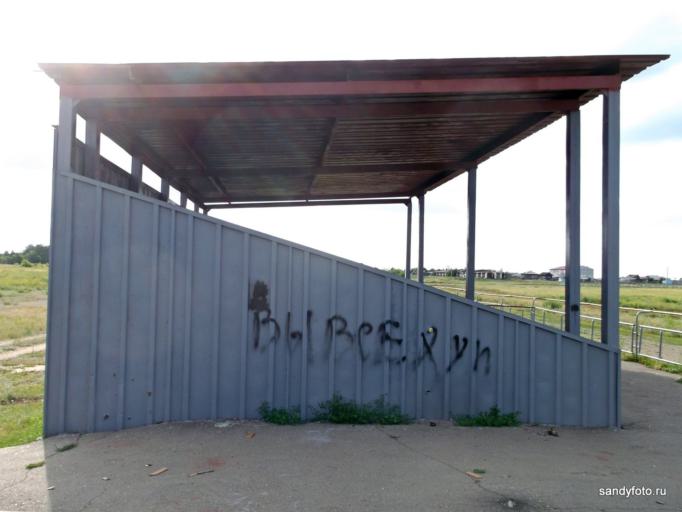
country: RU
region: Chelyabinsk
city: Troitsk
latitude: 54.0801
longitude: 61.5172
